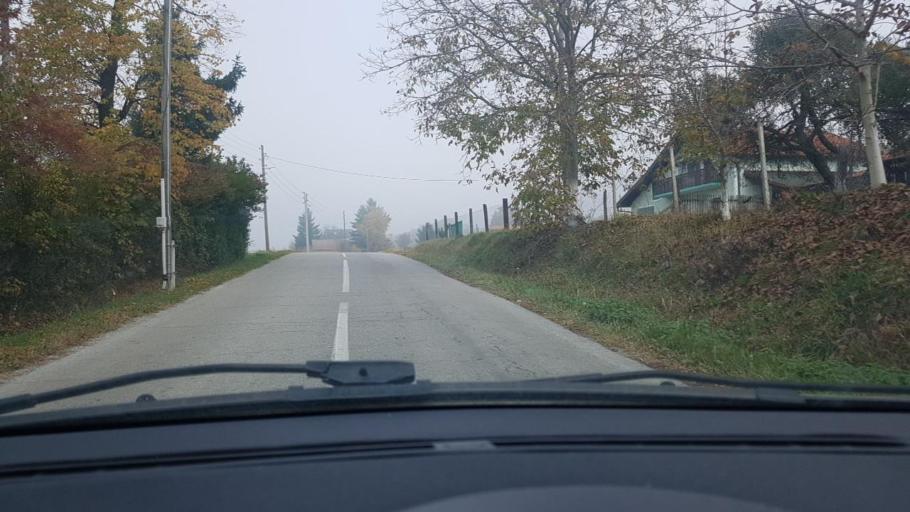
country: HR
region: Krapinsko-Zagorska
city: Zlatar
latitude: 46.1220
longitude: 16.1146
